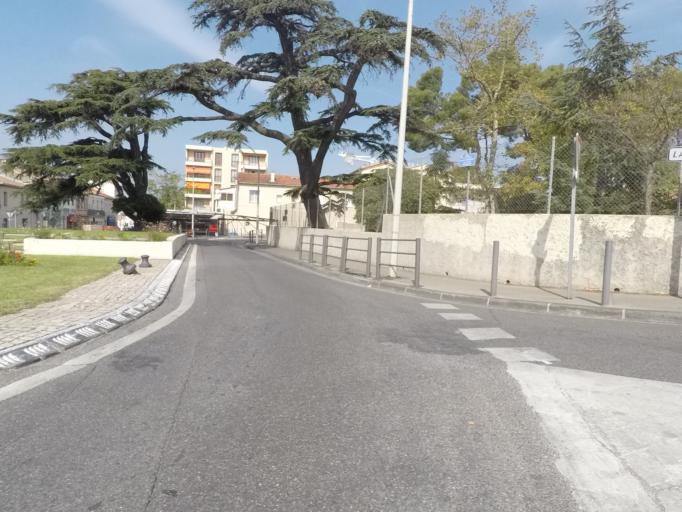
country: FR
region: Provence-Alpes-Cote d'Azur
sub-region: Departement des Bouches-du-Rhone
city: Marseille 09
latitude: 43.2570
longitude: 5.4192
